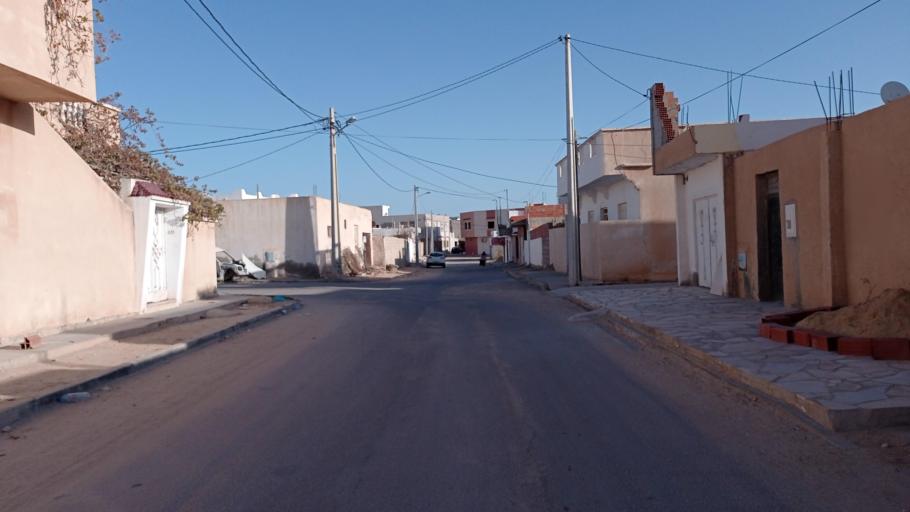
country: TN
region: Qabis
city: Gabes
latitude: 33.8545
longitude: 10.1208
